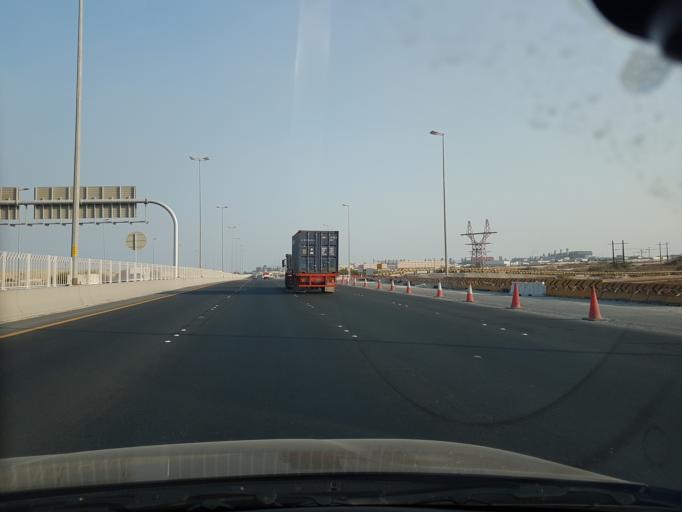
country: BH
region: Northern
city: Ar Rifa'
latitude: 26.1138
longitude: 50.5958
